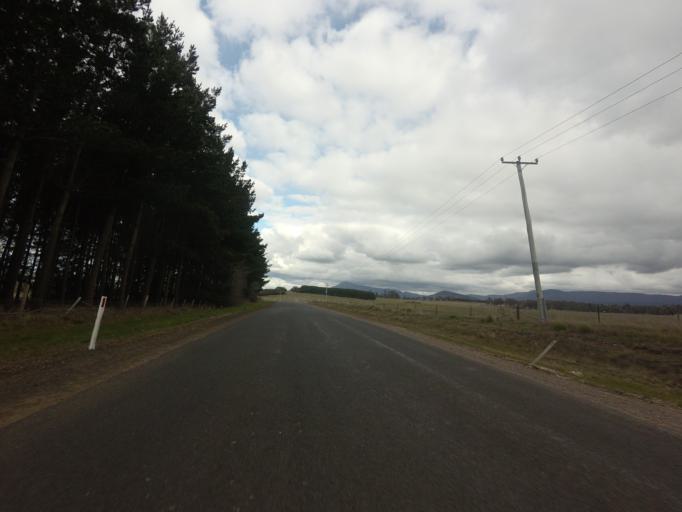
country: AU
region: Tasmania
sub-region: Northern Midlands
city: Longford
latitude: -41.7724
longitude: 147.0896
